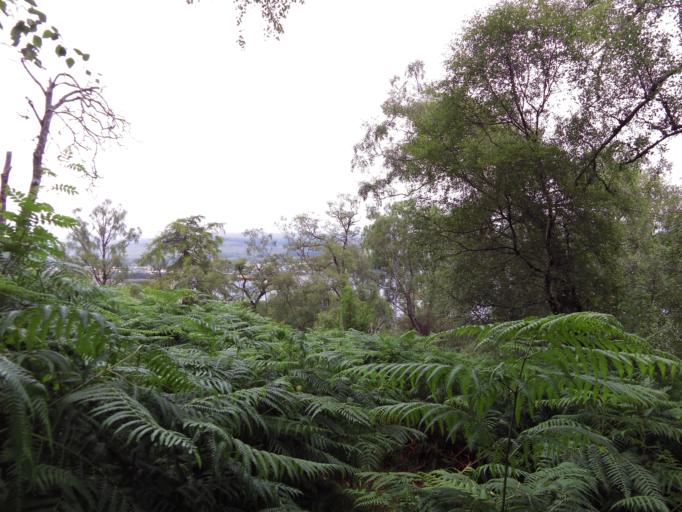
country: GB
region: Scotland
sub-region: Highland
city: Fort William
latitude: 56.8315
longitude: -5.1305
